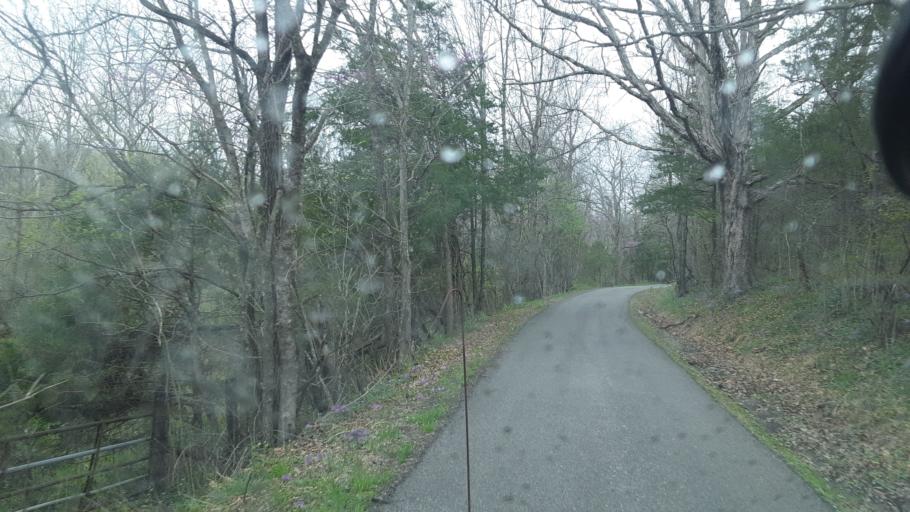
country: US
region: Kentucky
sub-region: Owen County
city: Owenton
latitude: 38.6462
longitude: -84.7883
